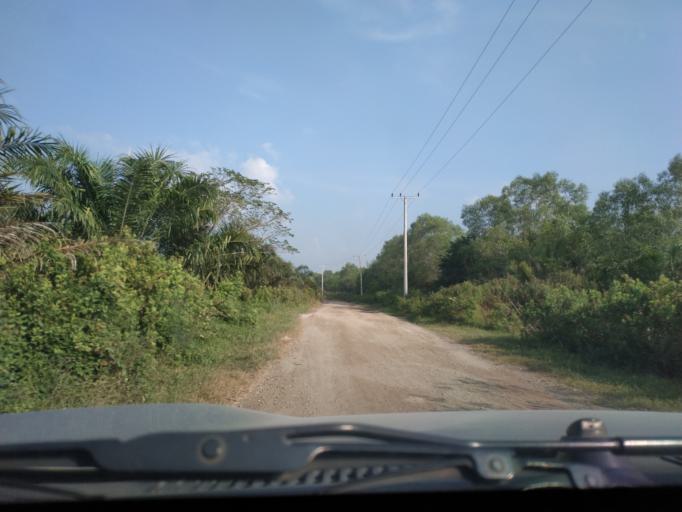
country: ID
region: North Sumatra
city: Teluk Nibung
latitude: 3.0872
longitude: 99.7884
